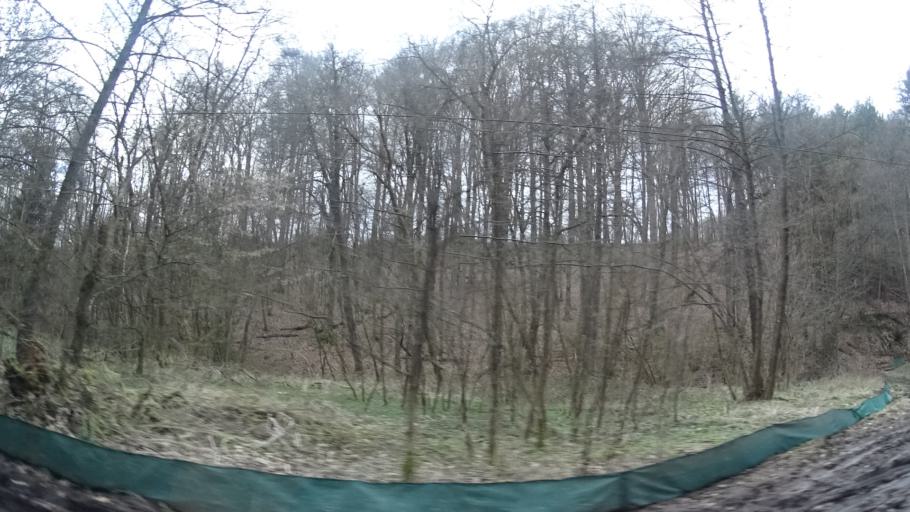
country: DE
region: Hesse
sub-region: Regierungsbezirk Darmstadt
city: Wiesbaden
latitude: 50.1137
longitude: 8.2610
